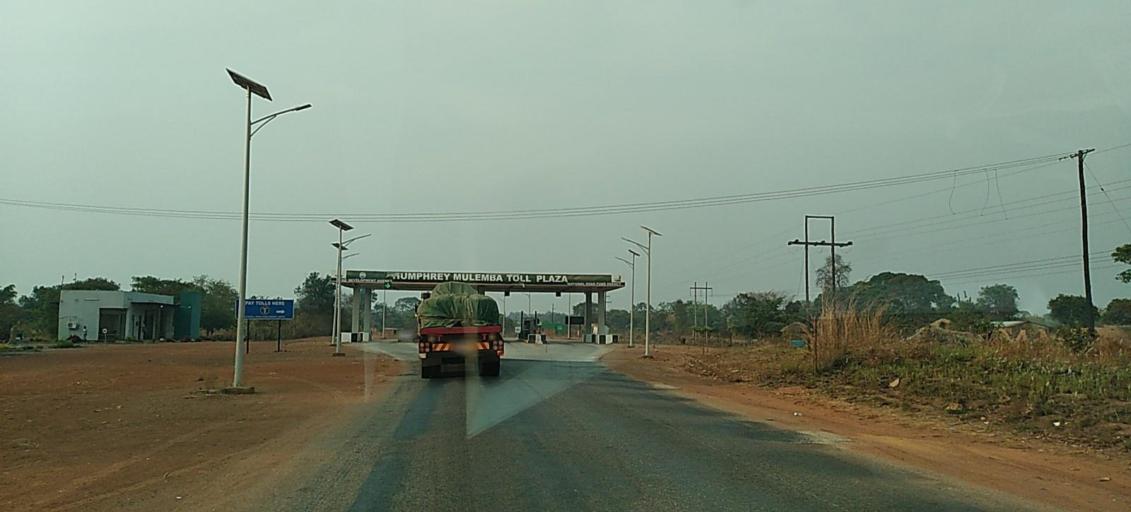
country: ZM
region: North-Western
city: Solwezi
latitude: -12.3158
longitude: 26.2701
